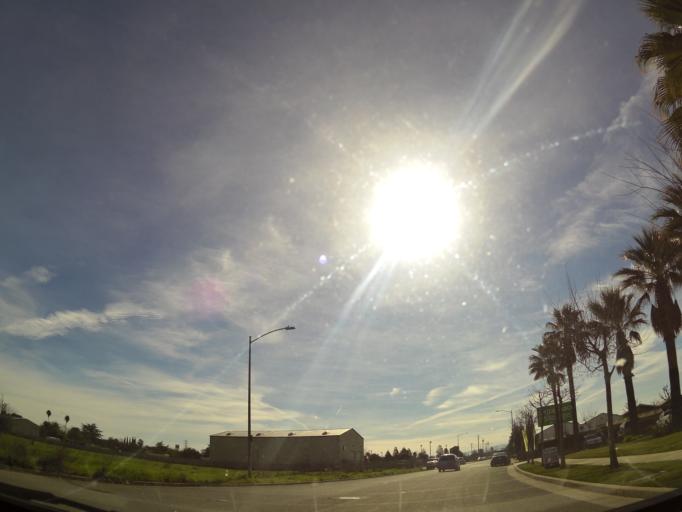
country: US
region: California
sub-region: Santa Clara County
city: Gilroy
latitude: 37.0244
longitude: -121.5738
